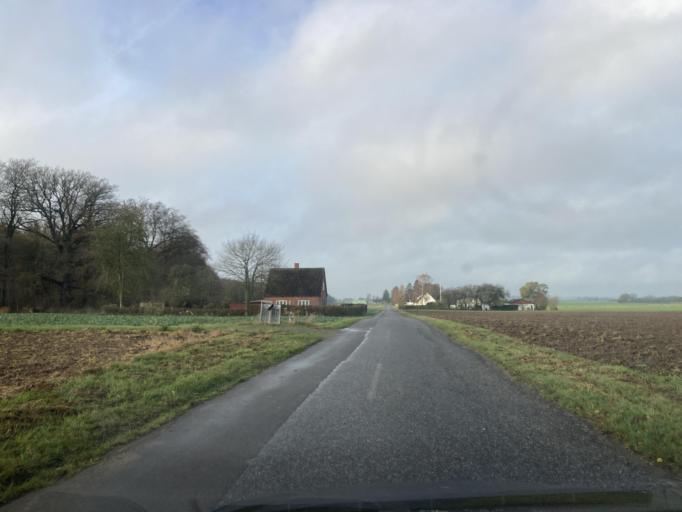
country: DK
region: Zealand
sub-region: Lolland Kommune
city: Rodby
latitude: 54.7927
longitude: 11.3559
